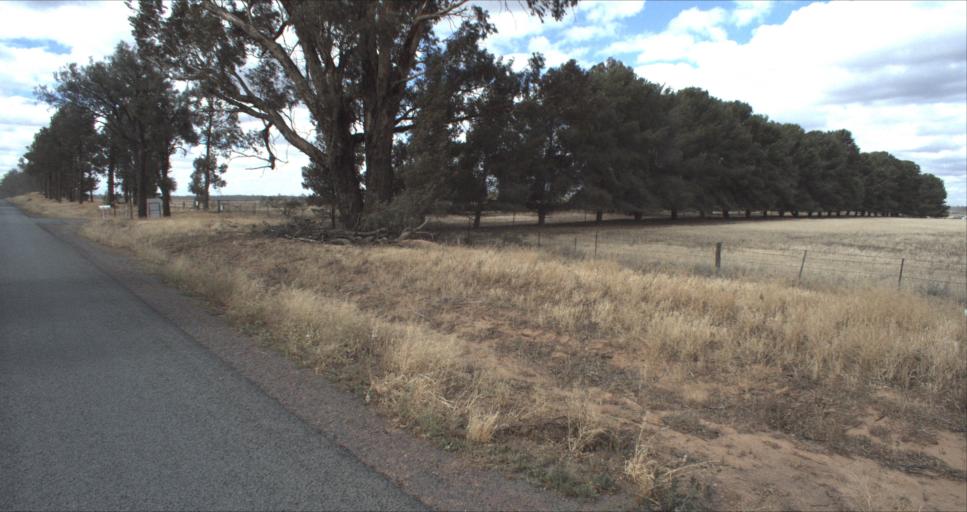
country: AU
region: New South Wales
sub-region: Leeton
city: Leeton
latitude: -34.6612
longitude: 146.3493
